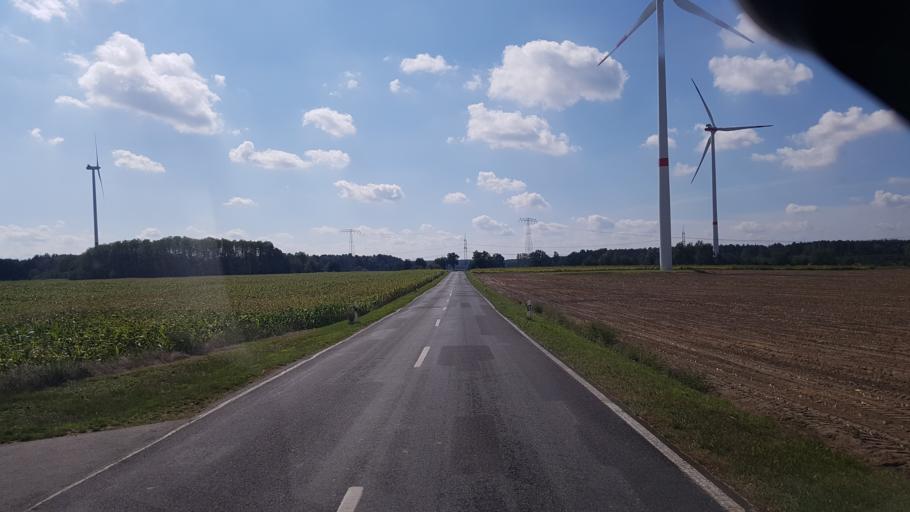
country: DE
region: Brandenburg
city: Drebkau
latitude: 51.6584
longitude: 14.2816
